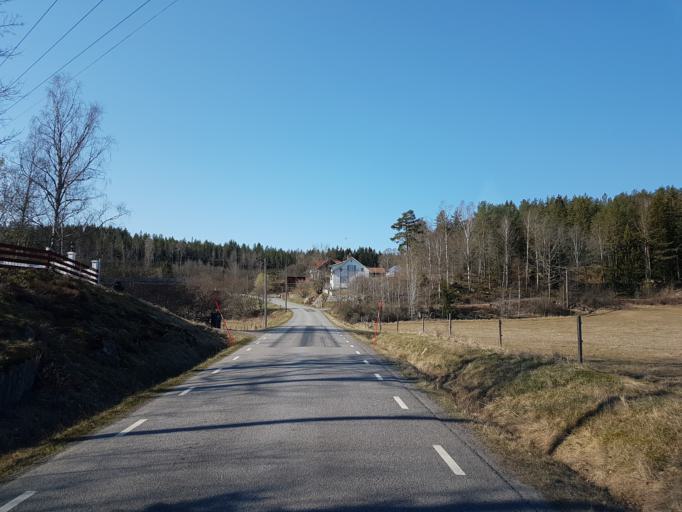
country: SE
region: OEstergoetland
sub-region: Valdemarsviks Kommun
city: Gusum
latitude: 58.1905
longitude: 16.3097
